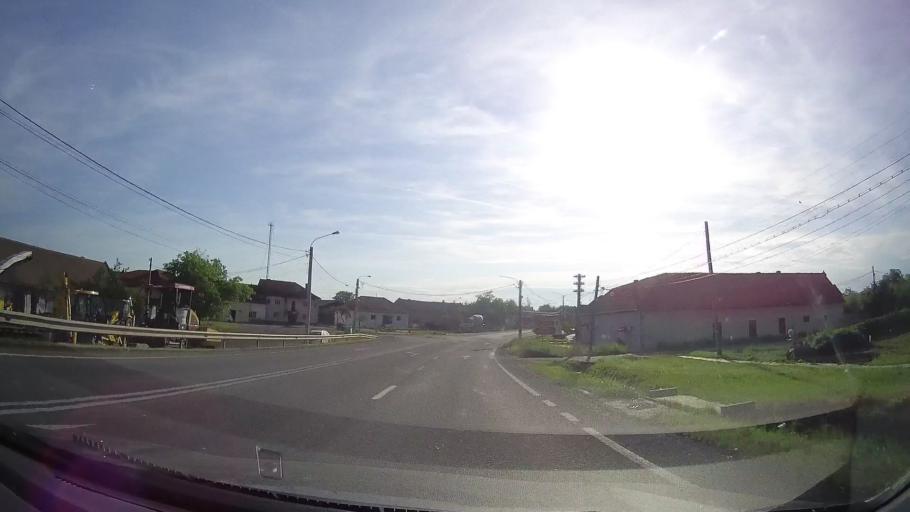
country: RO
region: Timis
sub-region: Comuna Topolovatu Mare
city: Topolovatu Mare
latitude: 45.7741
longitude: 21.6249
